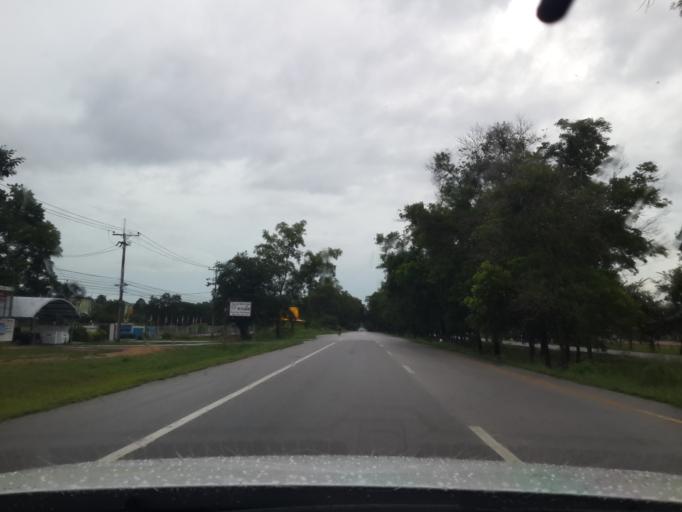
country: TH
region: Songkhla
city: Na Mom
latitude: 6.9852
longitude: 100.6591
